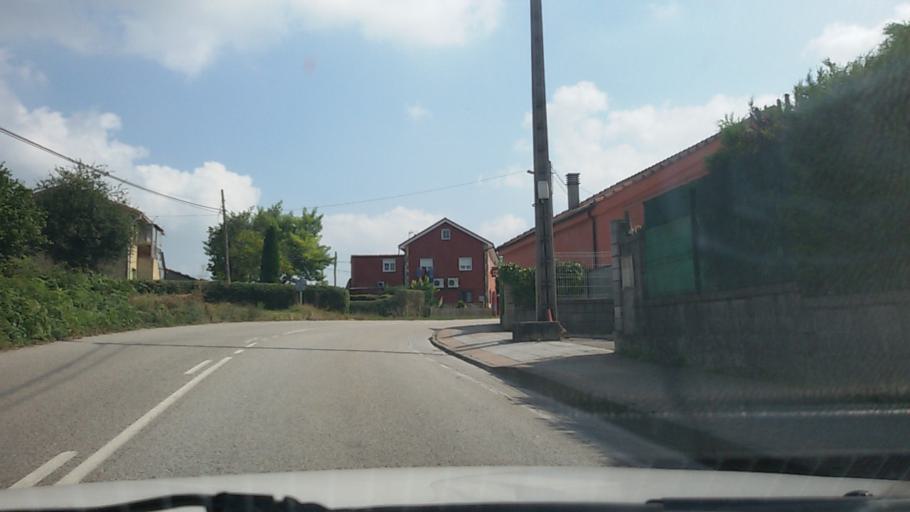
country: ES
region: Asturias
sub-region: Province of Asturias
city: Lugones
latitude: 43.4407
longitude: -5.8107
